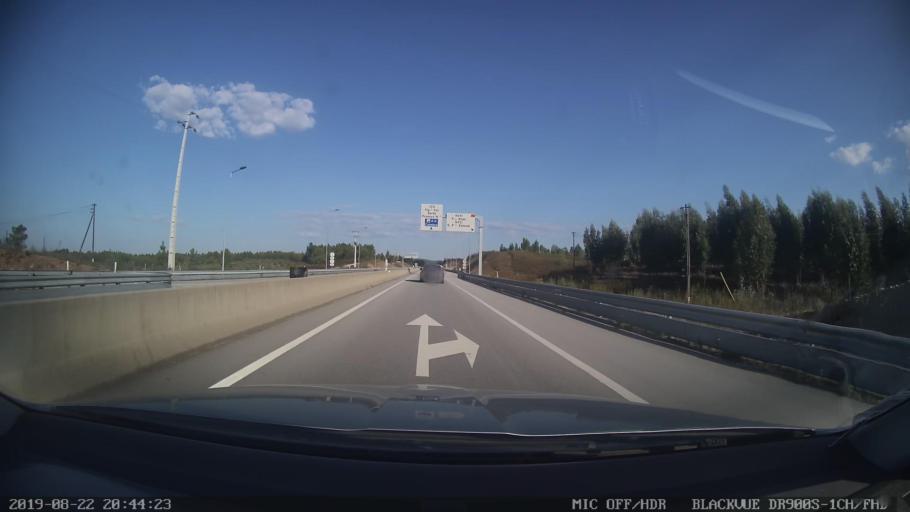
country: PT
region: Castelo Branco
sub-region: Proenca-A-Nova
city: Proenca-a-Nova
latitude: 39.7069
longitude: -7.8503
